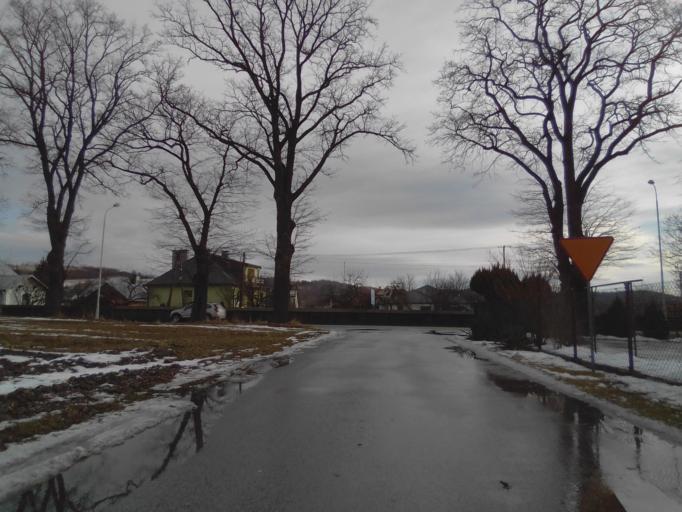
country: PL
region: Subcarpathian Voivodeship
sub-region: Powiat przemyski
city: Nienadowa
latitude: 49.8191
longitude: 22.4204
